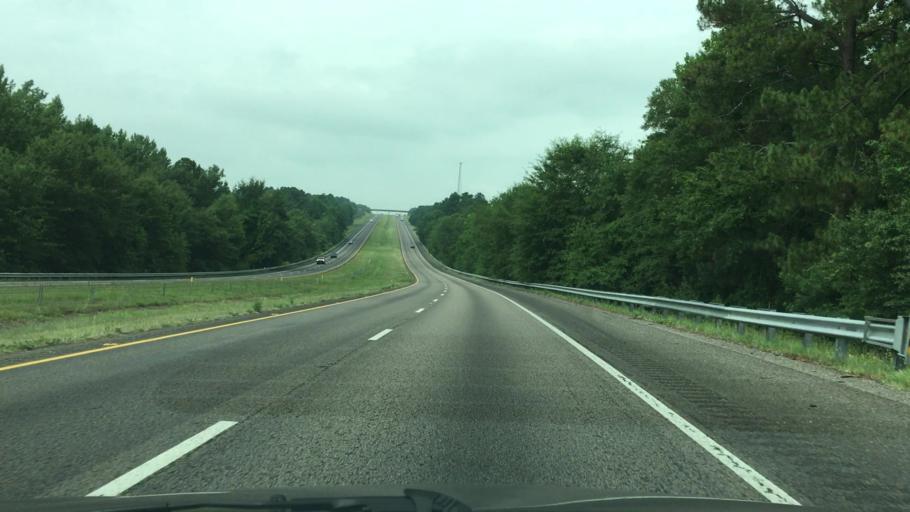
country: US
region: South Carolina
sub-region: Aiken County
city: Graniteville
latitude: 33.5993
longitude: -81.8678
